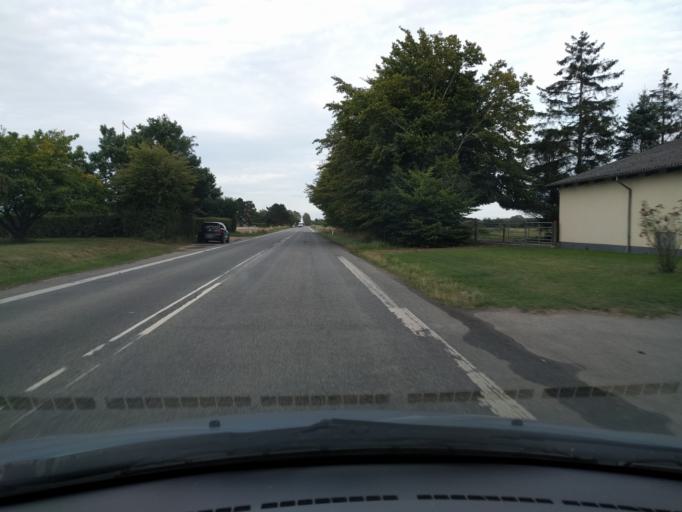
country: DK
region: Zealand
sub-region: Guldborgsund Kommune
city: Stubbekobing
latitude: 54.8937
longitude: 11.9866
